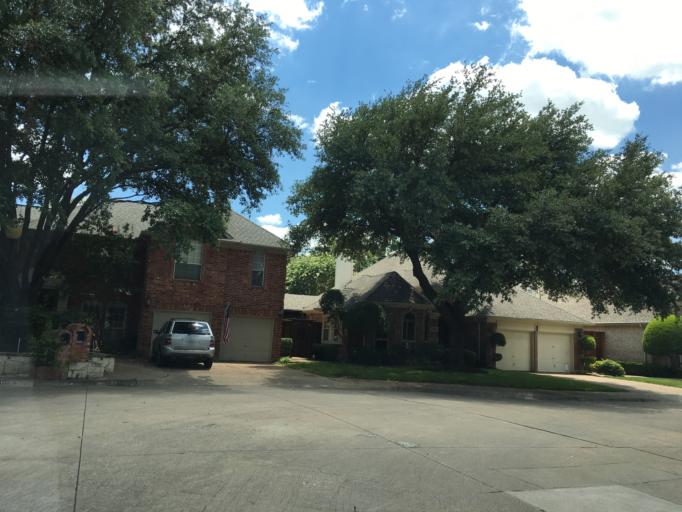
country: US
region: Texas
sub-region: Dallas County
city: Addison
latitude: 32.9441
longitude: -96.8443
